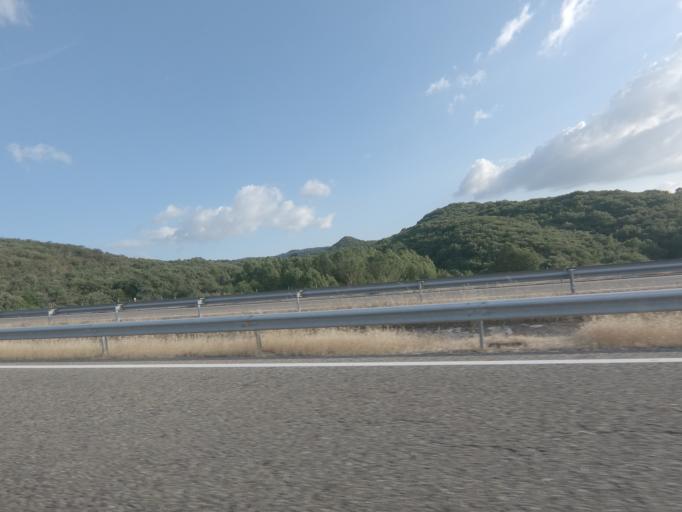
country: ES
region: Galicia
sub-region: Provincia de Ourense
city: Cualedro
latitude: 42.0092
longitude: -7.5698
